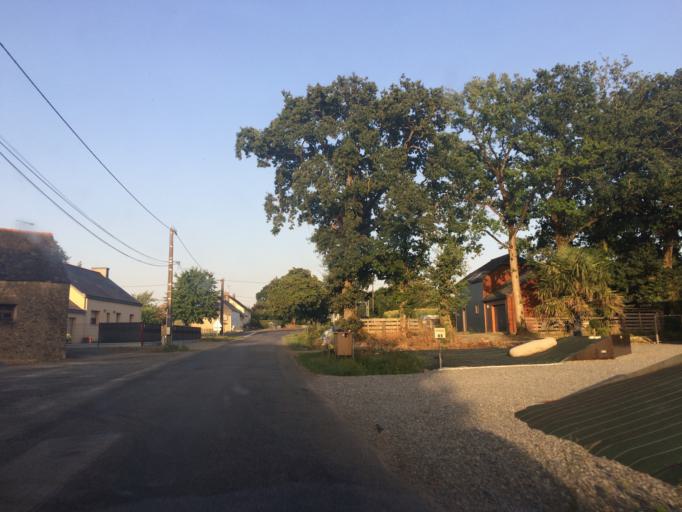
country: FR
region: Brittany
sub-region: Departement du Morbihan
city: Beganne
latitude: 47.6365
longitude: -2.2386
